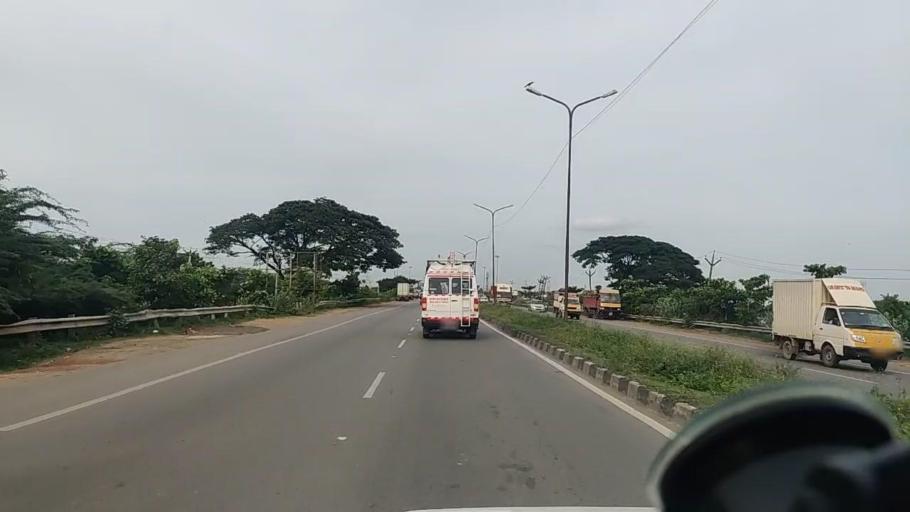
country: IN
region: Tamil Nadu
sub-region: Thiruvallur
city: Chinnasekkadu
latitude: 13.1751
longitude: 80.2407
